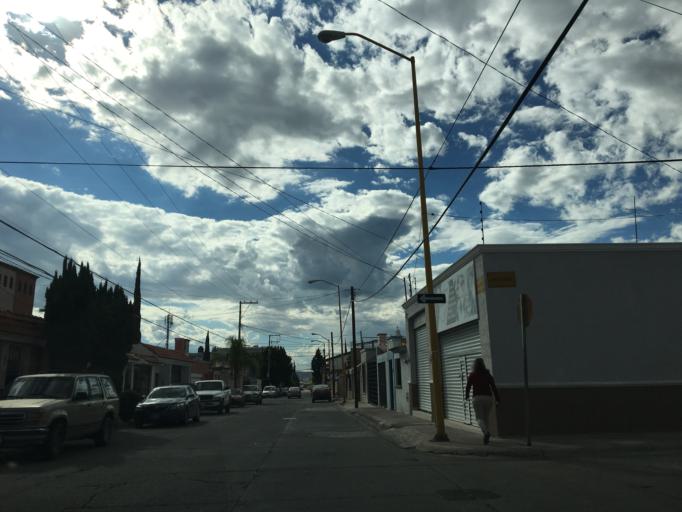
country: MX
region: Aguascalientes
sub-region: Jesus Maria
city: El Llano
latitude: 21.9285
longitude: -102.3037
